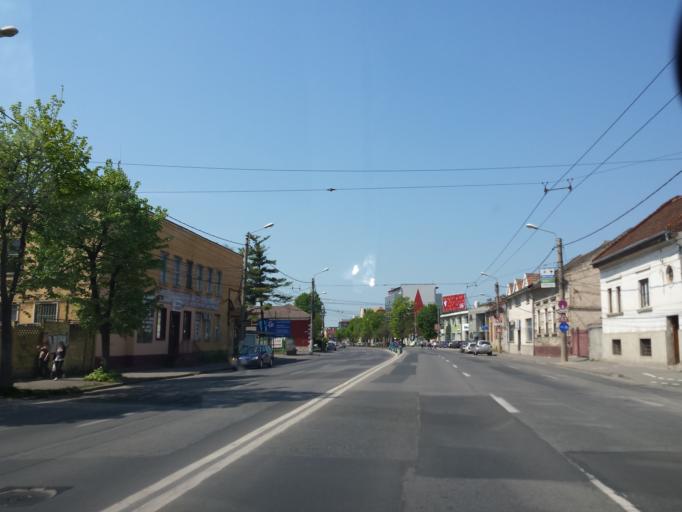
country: RO
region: Timis
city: Timisoara
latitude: 45.7637
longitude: 21.2535
